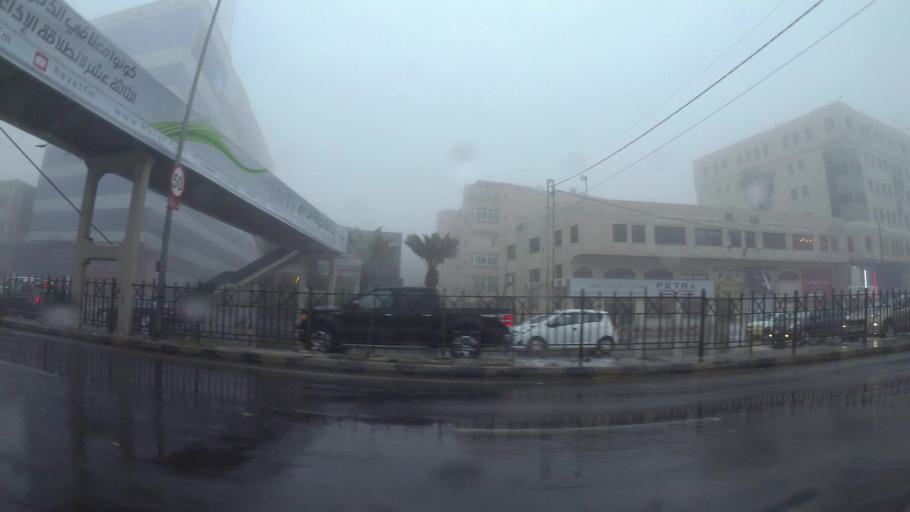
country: JO
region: Amman
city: Al Jubayhah
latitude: 31.9932
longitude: 35.8701
